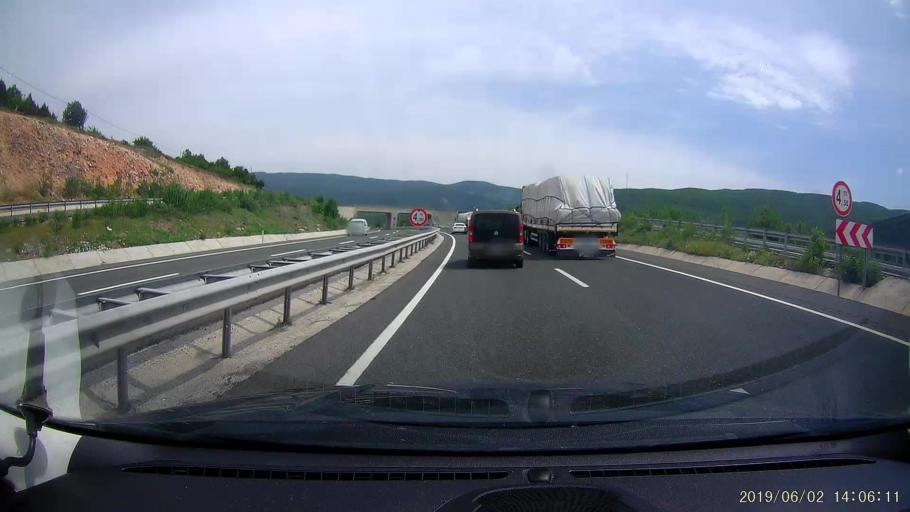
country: TR
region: Cankiri
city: Ilgaz
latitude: 40.8918
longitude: 33.6772
